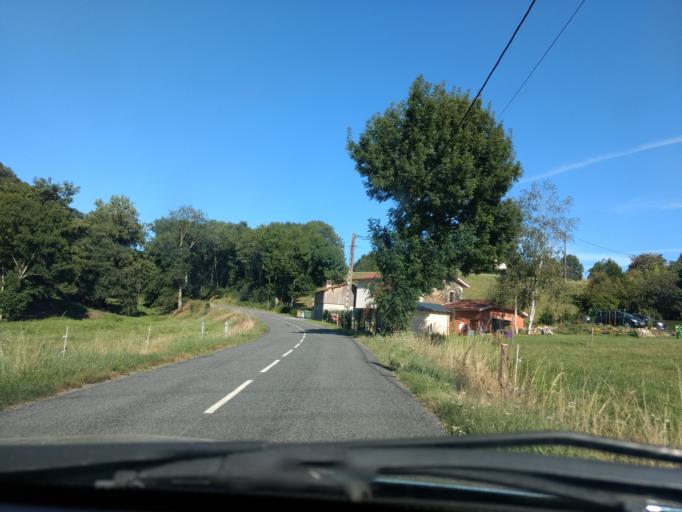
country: FR
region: Midi-Pyrenees
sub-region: Departement de l'Aveyron
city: Livinhac-le-Haut
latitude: 44.6152
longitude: 2.1857
